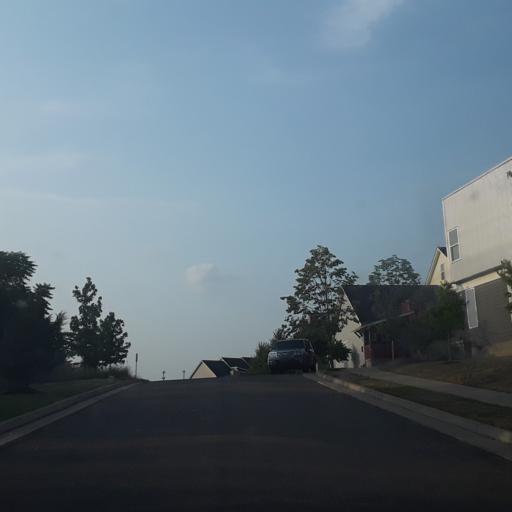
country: US
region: Tennessee
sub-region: Williamson County
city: Brentwood Estates
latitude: 36.0403
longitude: -86.7229
